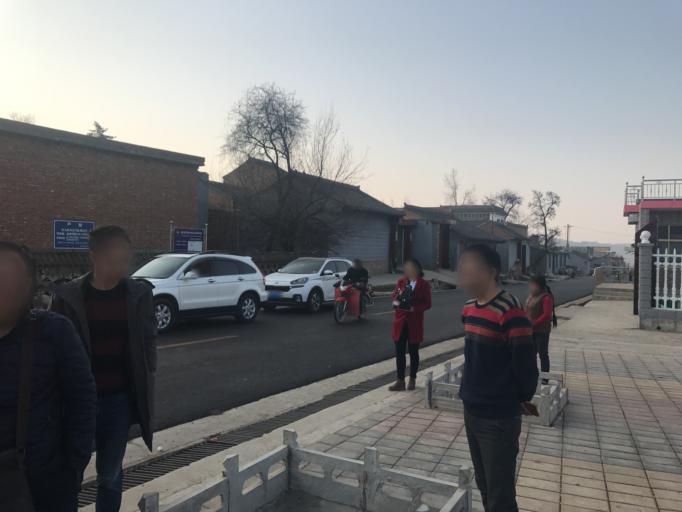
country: CN
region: Gansu Sheng
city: Maji
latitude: 35.3978
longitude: 103.0582
